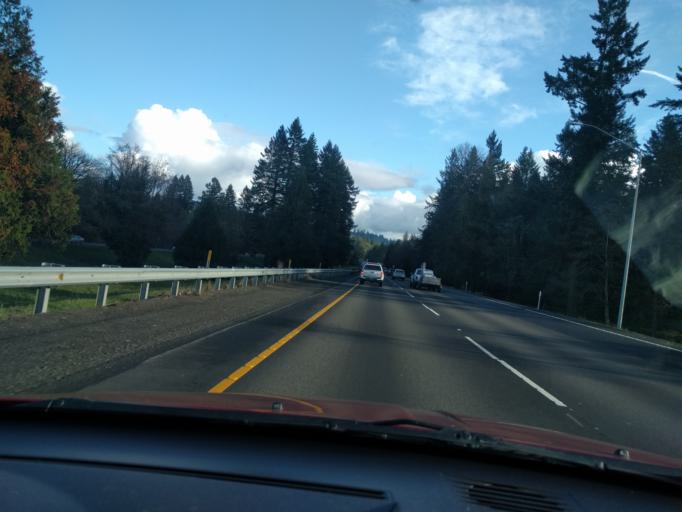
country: US
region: Oregon
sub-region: Clackamas County
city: Stafford
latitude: 45.3678
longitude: -122.6981
